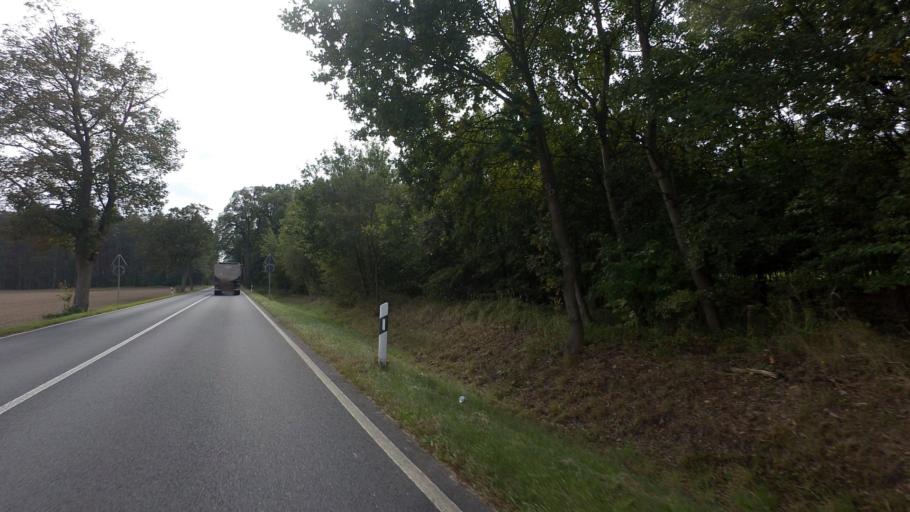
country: DE
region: Brandenburg
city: Kasel-Golzig
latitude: 51.8937
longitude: 13.6844
